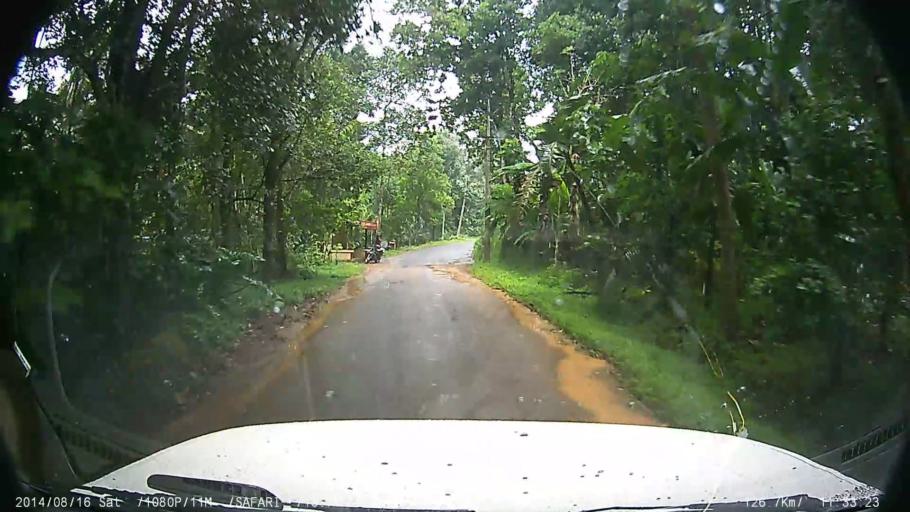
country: IN
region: Kerala
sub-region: Kottayam
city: Palackattumala
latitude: 9.7754
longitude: 76.5560
